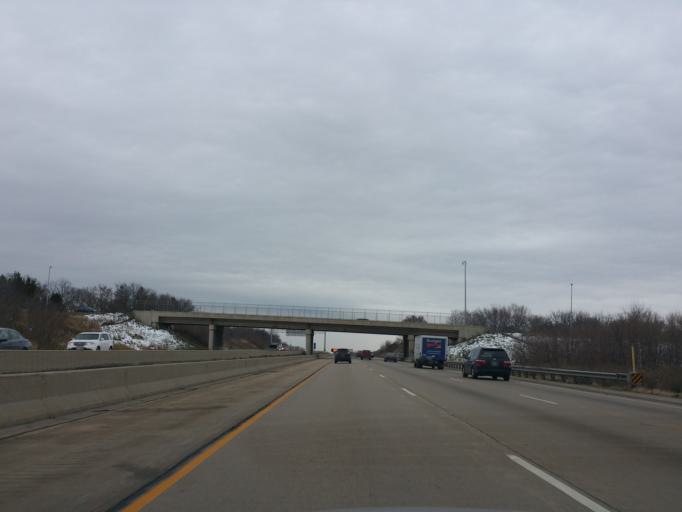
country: US
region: Wisconsin
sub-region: Dane County
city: Monona
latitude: 43.0860
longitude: -89.2843
